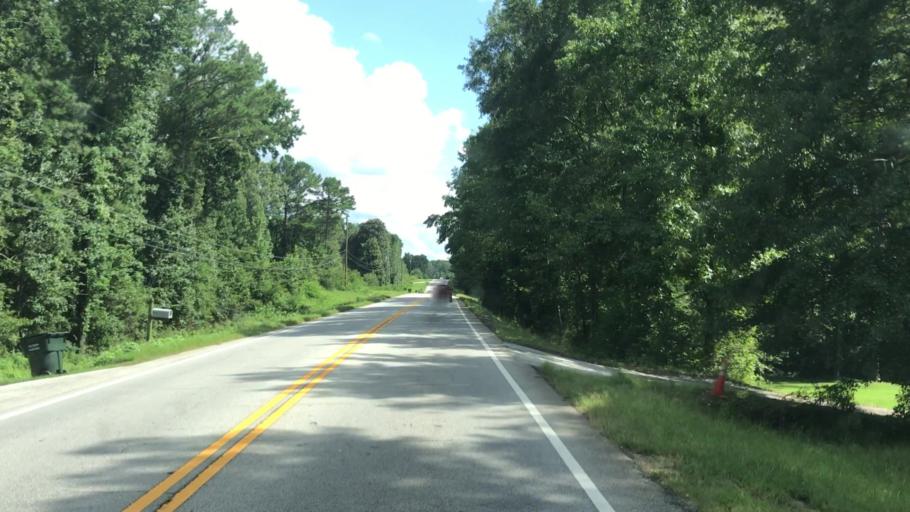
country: US
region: Georgia
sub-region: Walton County
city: Walnut Grove
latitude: 33.7095
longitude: -83.8516
